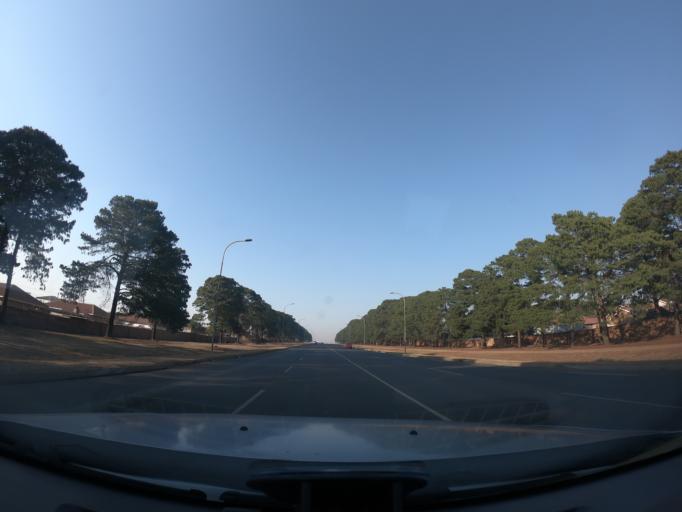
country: ZA
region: Mpumalanga
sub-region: Nkangala District Municipality
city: Middelburg
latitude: -25.7984
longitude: 29.4618
